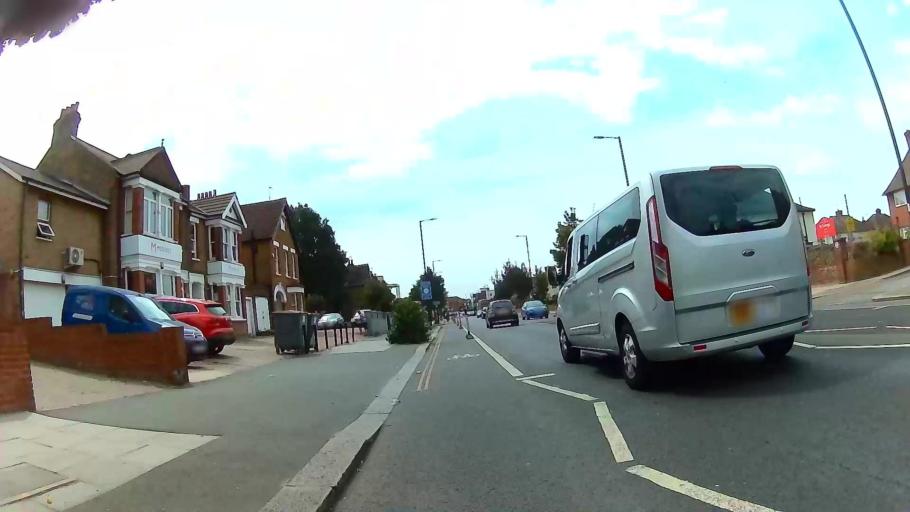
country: GB
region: England
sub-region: Hertfordshire
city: Waltham Cross
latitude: 51.6735
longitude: -0.0386
